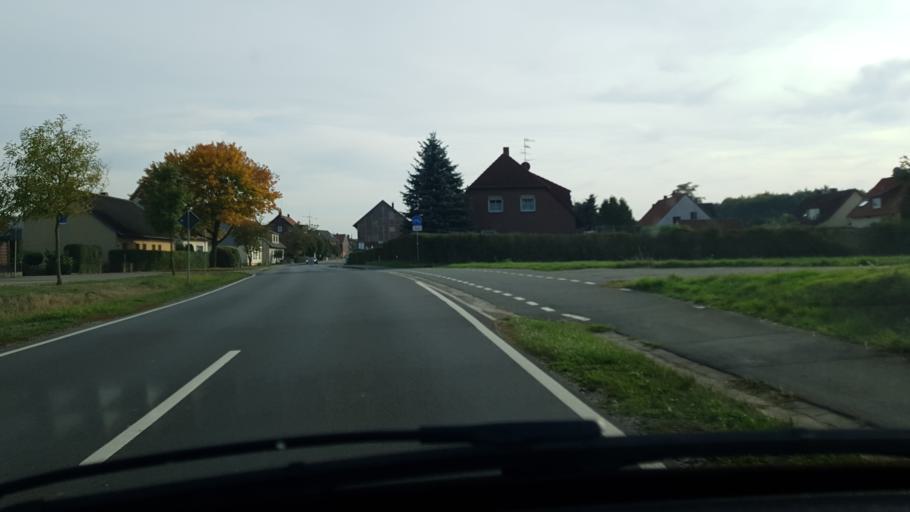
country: DE
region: Lower Saxony
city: Lehre
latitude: 52.3082
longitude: 10.6578
